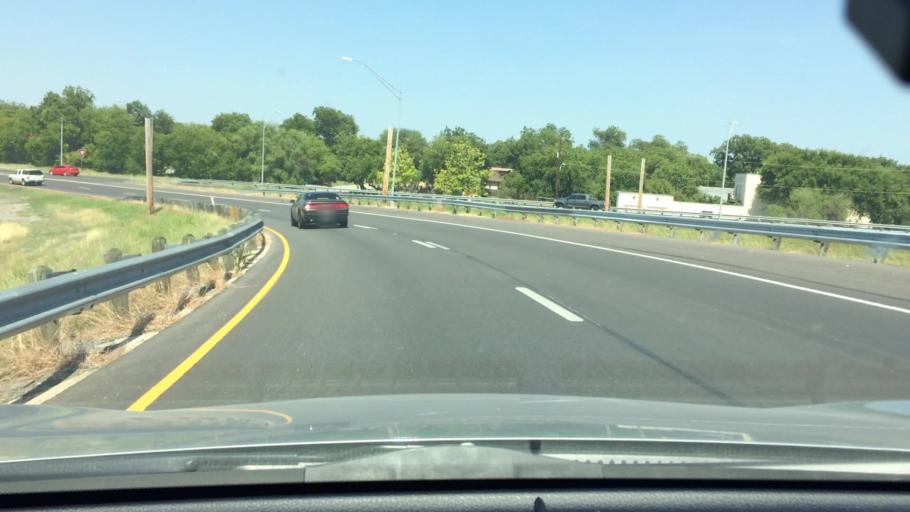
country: US
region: Texas
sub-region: Bexar County
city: San Antonio
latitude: 29.3949
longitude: -98.4769
